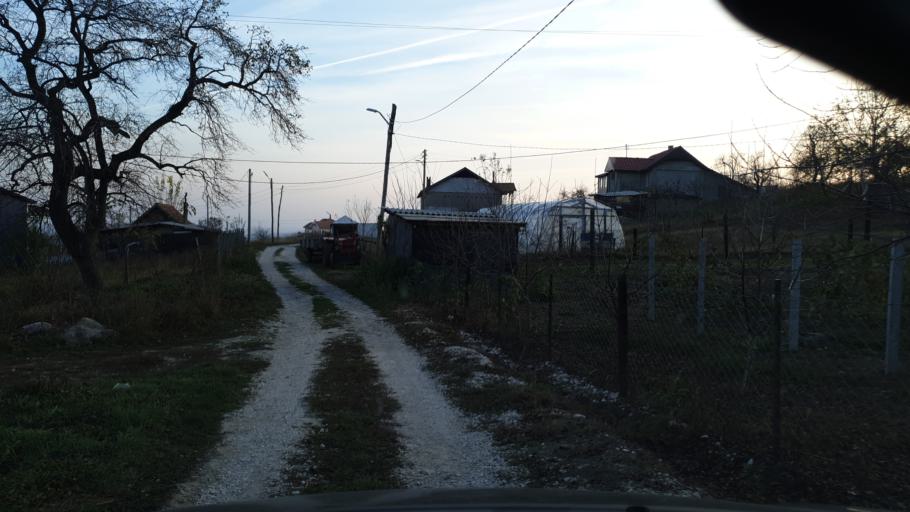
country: RS
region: Central Serbia
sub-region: Borski Okrug
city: Bor
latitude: 44.0610
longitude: 22.0898
